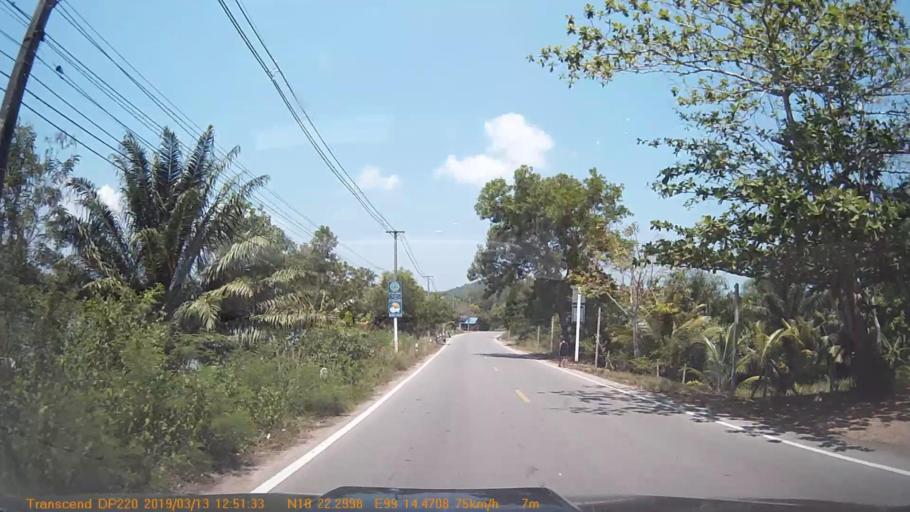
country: TH
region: Chumphon
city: Chumphon
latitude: 10.3721
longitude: 99.2412
